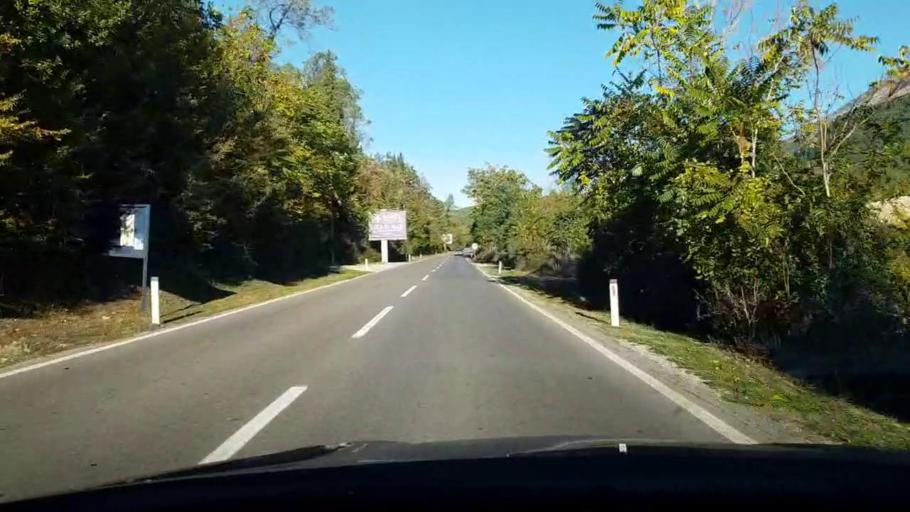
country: ME
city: Igalo
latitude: 42.4768
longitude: 18.4639
